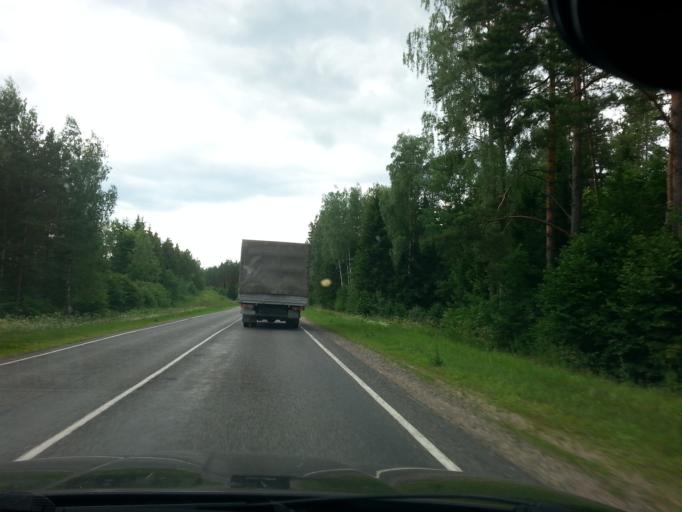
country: BY
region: Minsk
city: Svir
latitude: 54.8559
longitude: 26.2967
